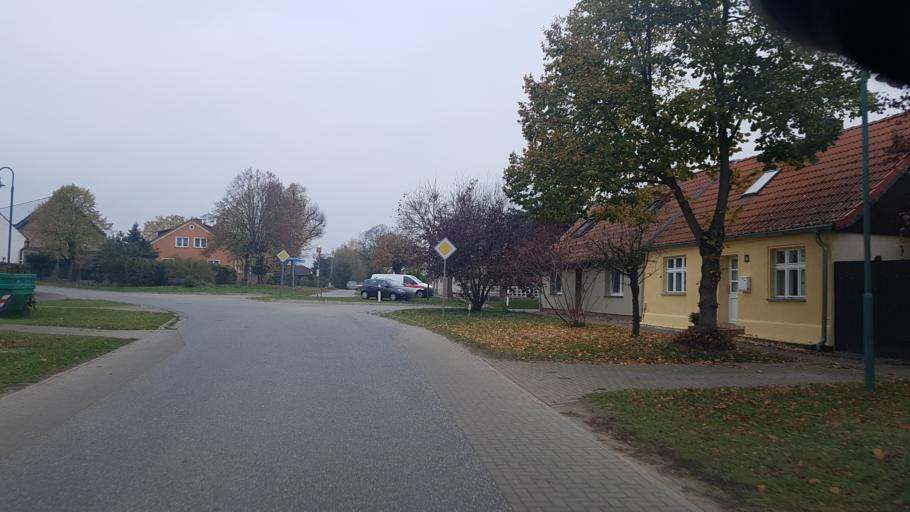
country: DE
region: Brandenburg
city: Schonermark
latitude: 52.9336
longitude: 13.1017
